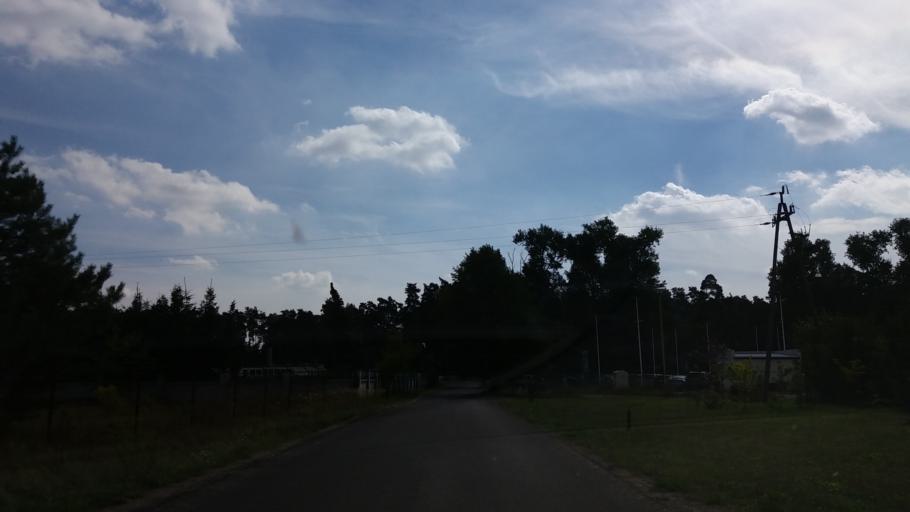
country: PL
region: West Pomeranian Voivodeship
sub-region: Powiat stargardzki
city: Kobylanka
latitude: 53.3528
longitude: 14.9088
